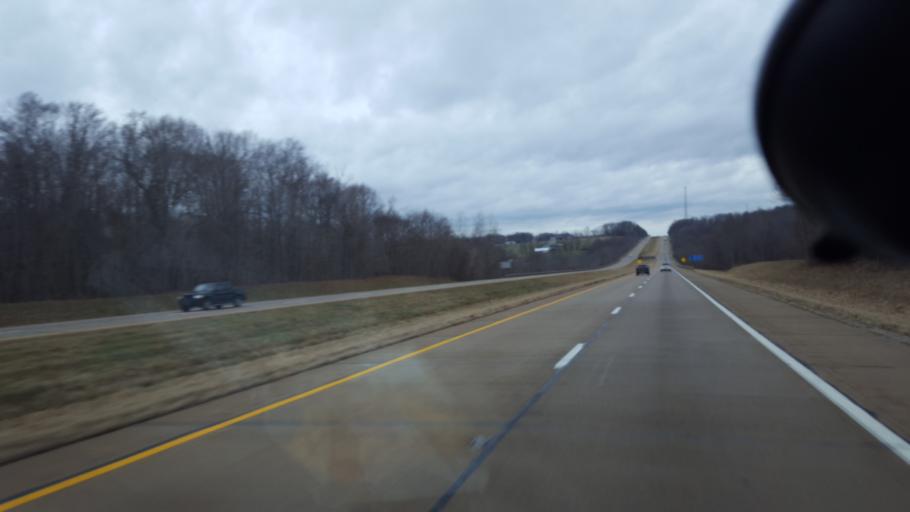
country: US
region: Ohio
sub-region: Ashland County
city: Ashland
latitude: 40.7851
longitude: -82.3187
